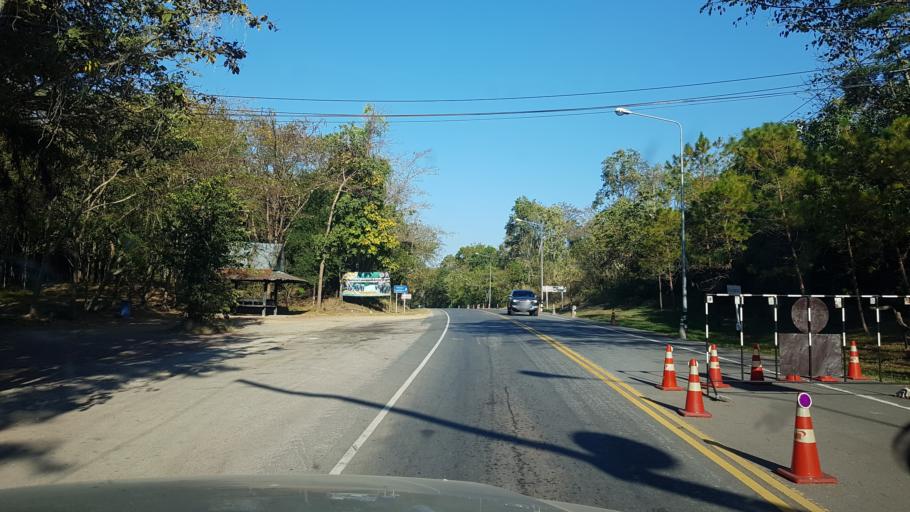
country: TH
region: Phetchabun
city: Lom Sak
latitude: 16.7371
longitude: 101.4395
